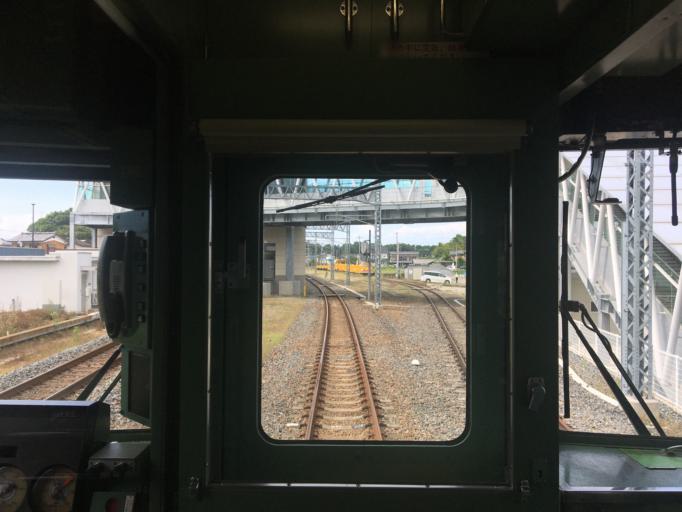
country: JP
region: Saitama
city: Yorii
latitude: 36.1070
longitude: 139.2344
